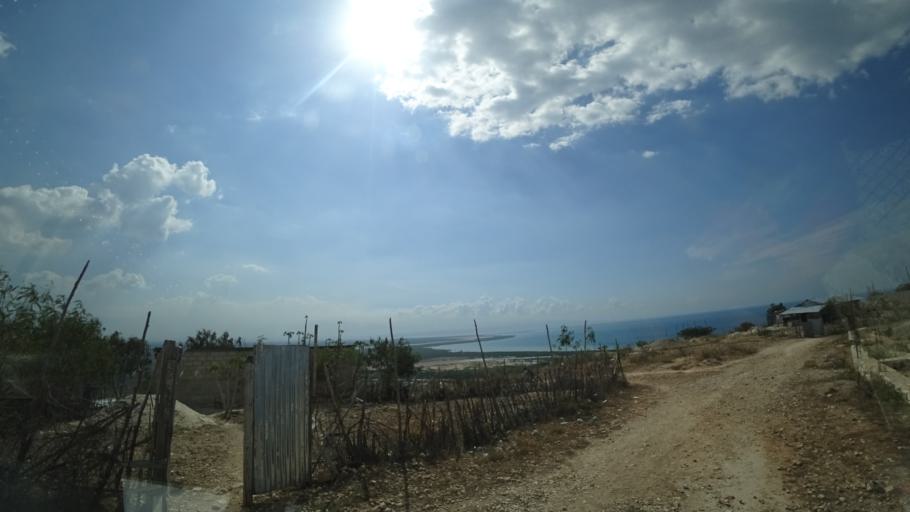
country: HT
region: Ouest
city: Cabaret
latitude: 18.6779
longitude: -72.3088
